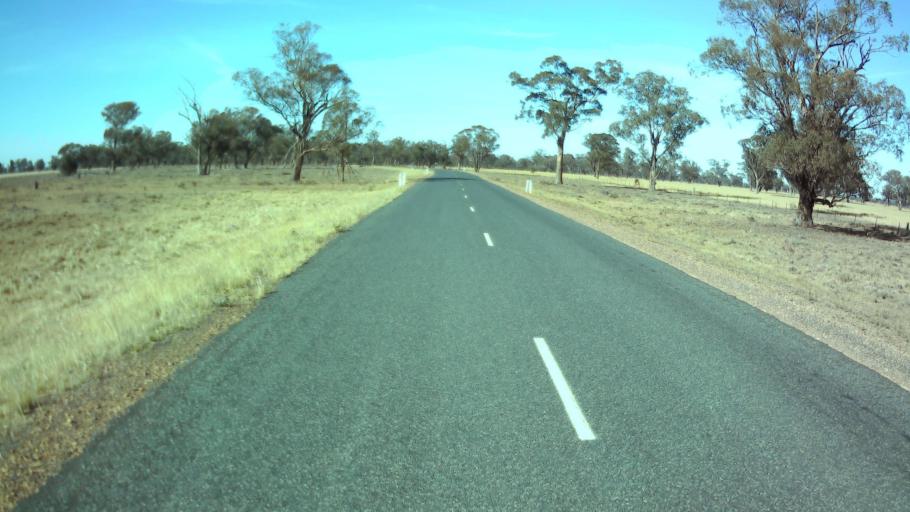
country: AU
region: New South Wales
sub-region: Weddin
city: Grenfell
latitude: -34.0572
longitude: 147.9129
